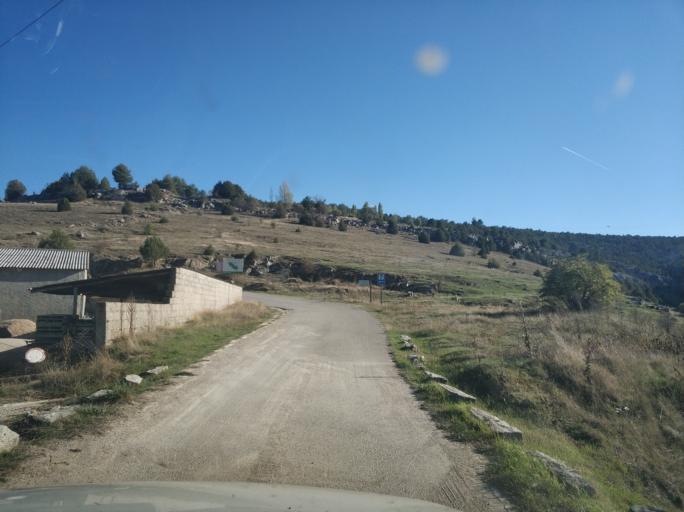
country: ES
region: Castille and Leon
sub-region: Provincia de Burgos
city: Hontoria del Pinar
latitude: 41.8442
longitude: -3.1653
